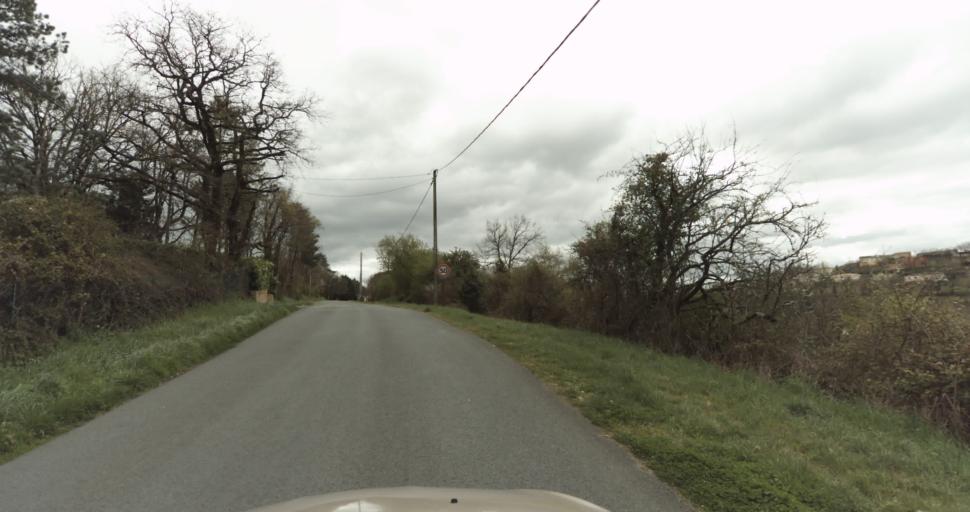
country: FR
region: Midi-Pyrenees
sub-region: Departement du Tarn
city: Puygouzon
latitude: 43.9032
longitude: 2.1724
